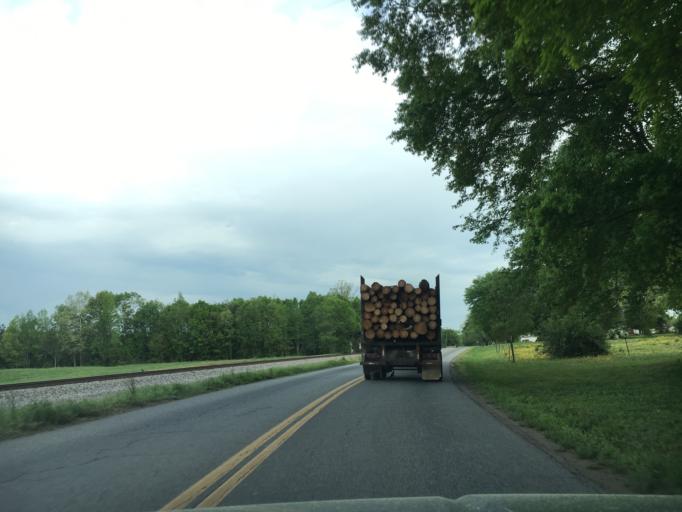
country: US
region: Virginia
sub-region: Halifax County
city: Halifax
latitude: 36.8984
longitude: -78.9079
